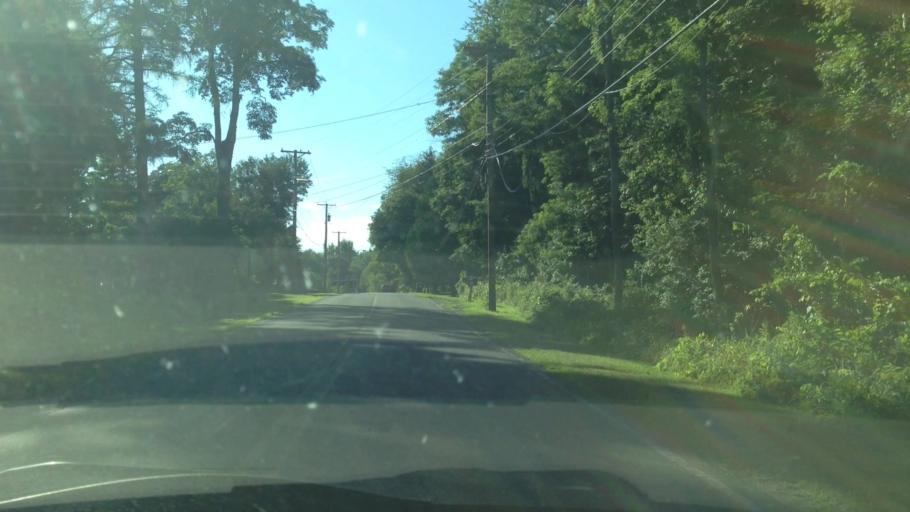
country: US
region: New York
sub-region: Ulster County
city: Clintondale
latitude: 41.7412
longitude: -74.0375
